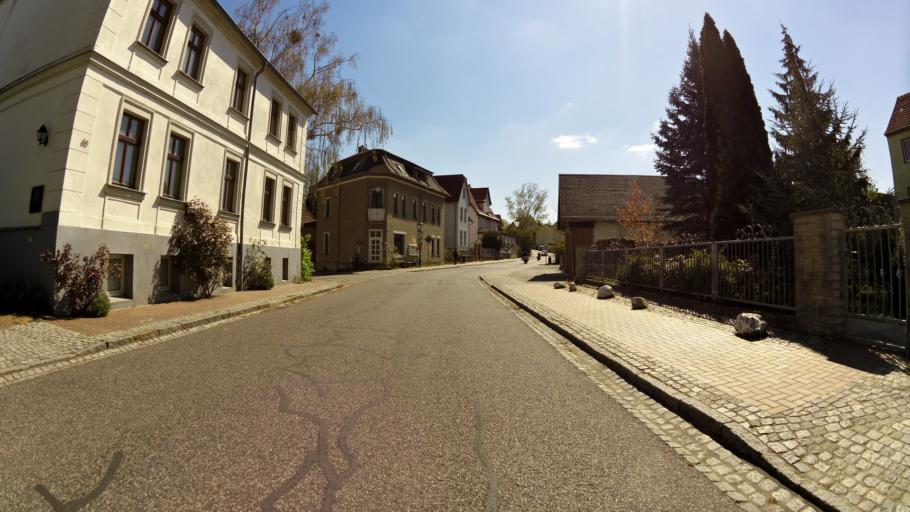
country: DE
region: Brandenburg
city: Buckow
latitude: 52.5634
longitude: 14.0749
